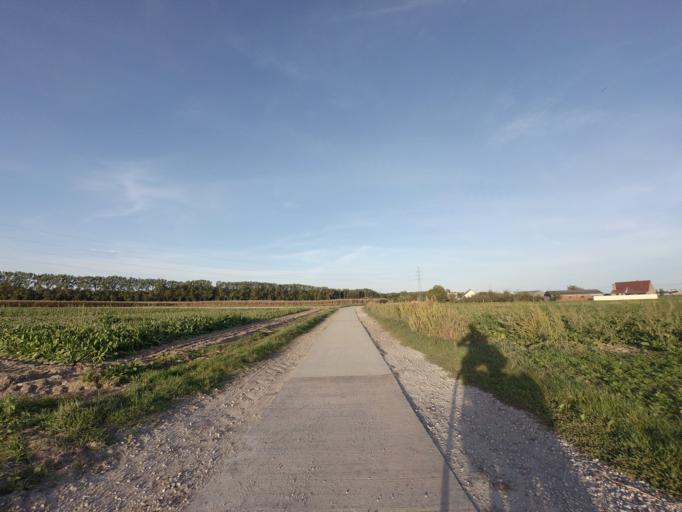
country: BE
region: Flanders
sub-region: Provincie Vlaams-Brabant
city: Haacht
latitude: 50.9487
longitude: 4.6136
